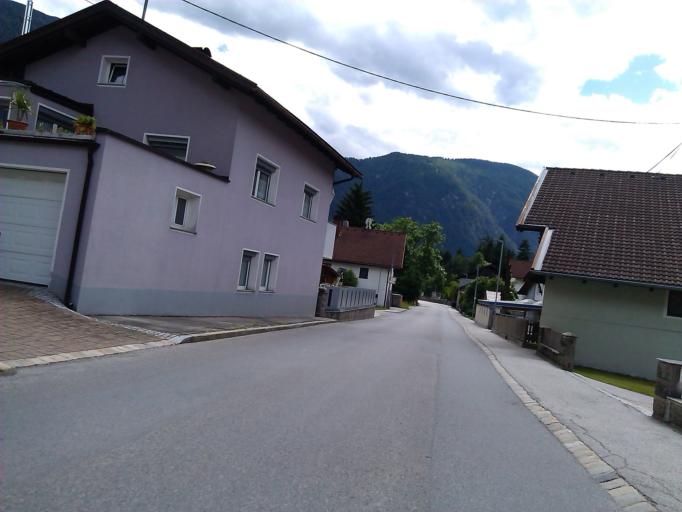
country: AT
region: Tyrol
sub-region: Politischer Bezirk Imst
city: Nassereith
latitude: 47.3107
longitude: 10.8398
